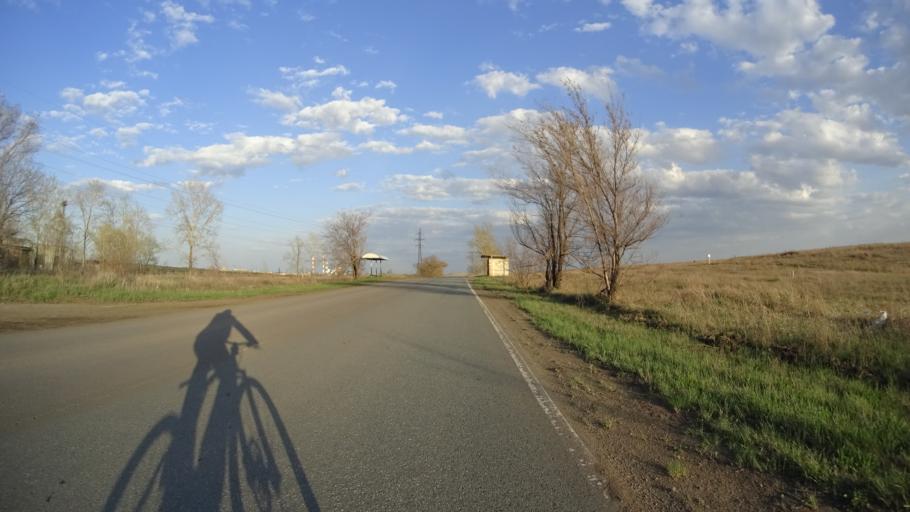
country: RU
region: Chelyabinsk
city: Troitsk
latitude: 54.0542
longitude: 61.5892
